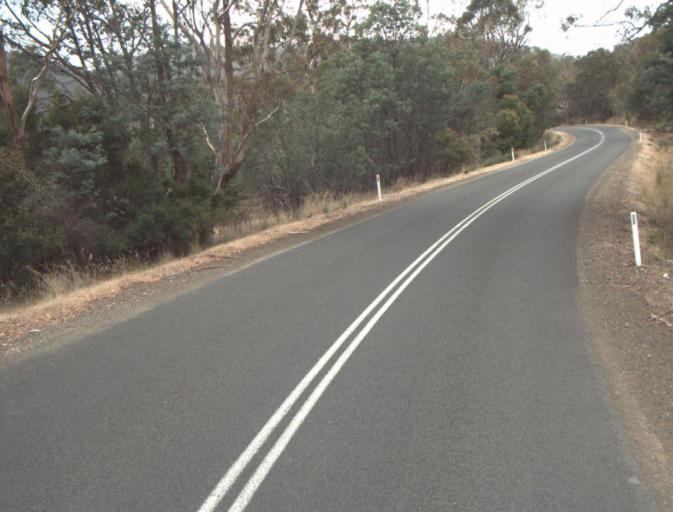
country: AU
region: Tasmania
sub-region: Northern Midlands
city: Evandale
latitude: -41.5012
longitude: 147.3811
